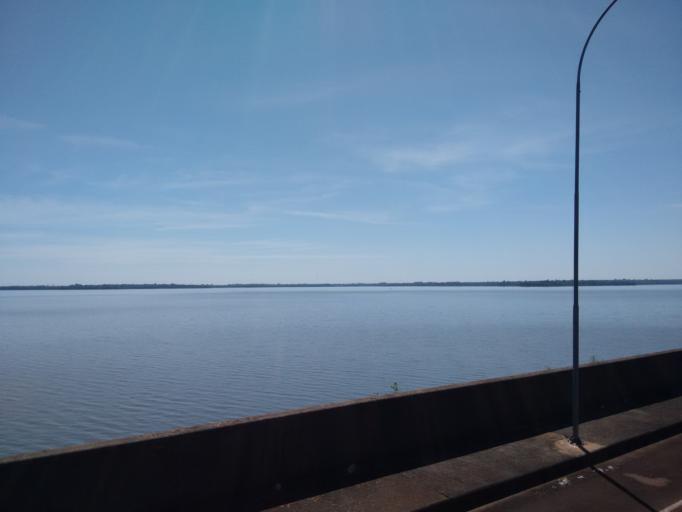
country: PY
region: Alto Parana
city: Ciudad del Este
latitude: -25.4188
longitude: -54.5694
